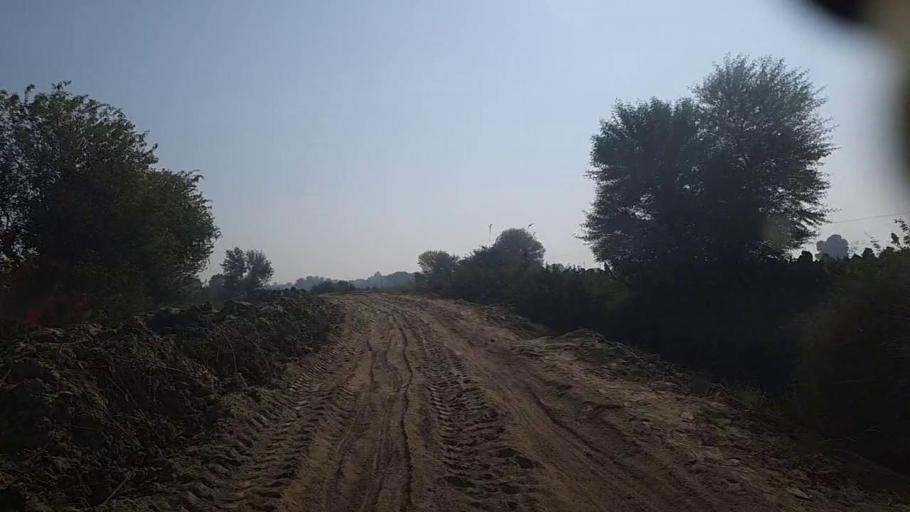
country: PK
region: Sindh
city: Kandiari
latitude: 27.0128
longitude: 68.5020
